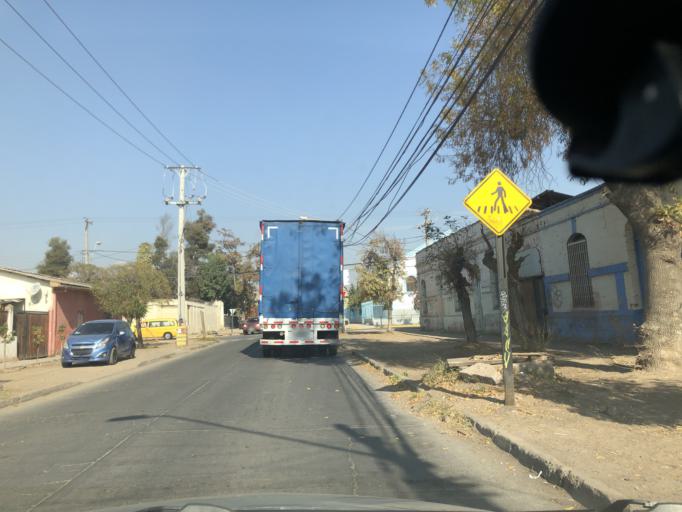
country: CL
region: Santiago Metropolitan
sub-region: Provincia de Cordillera
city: Puente Alto
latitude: -33.6076
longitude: -70.5675
